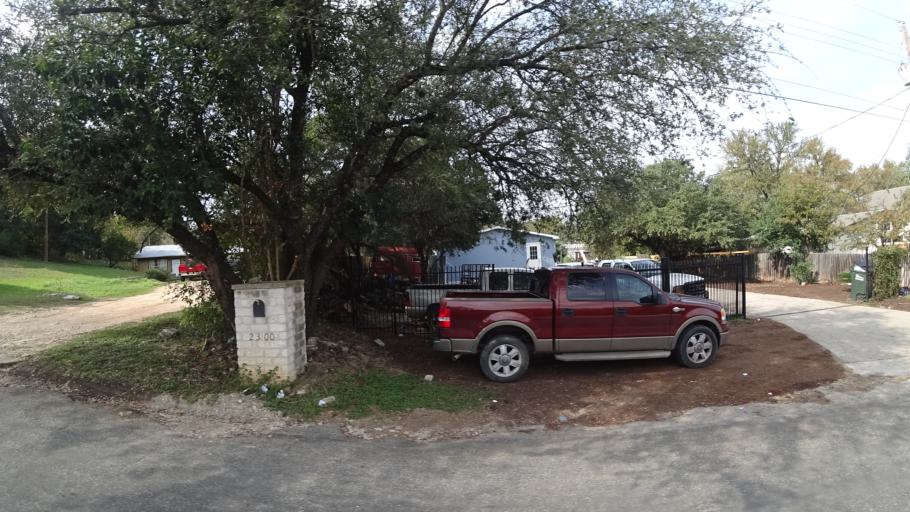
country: US
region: Texas
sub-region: Travis County
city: Hudson Bend
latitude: 30.3797
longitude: -97.9308
